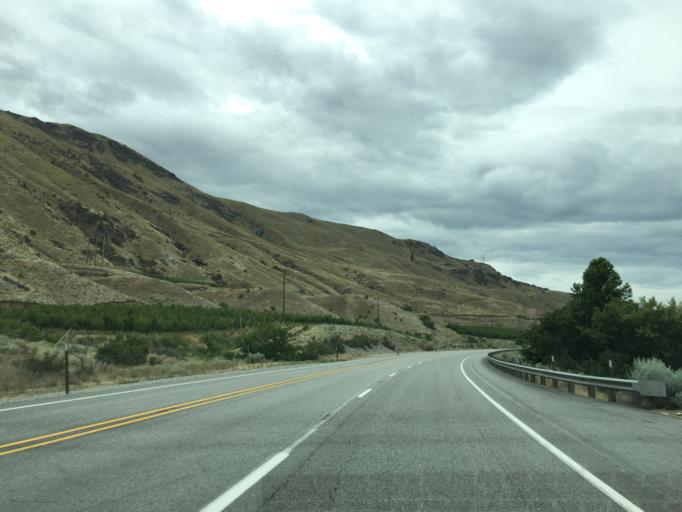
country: US
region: Washington
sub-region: Chelan County
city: Sunnyslope
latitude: 47.5500
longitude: -120.2538
